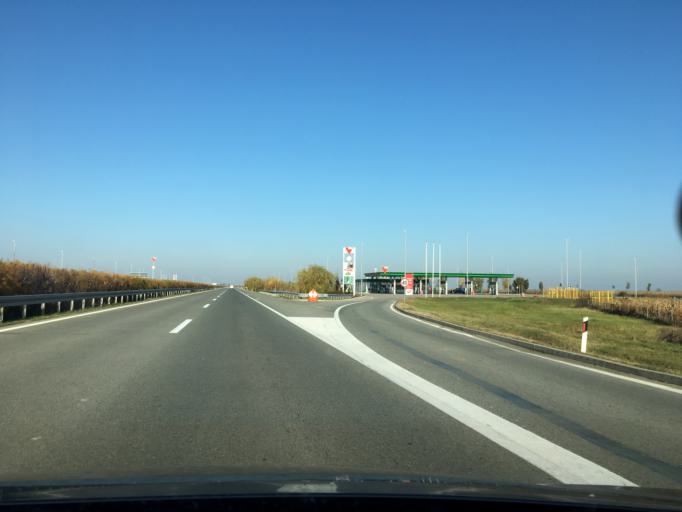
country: RS
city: Rumenka
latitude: 45.3269
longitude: 19.7825
